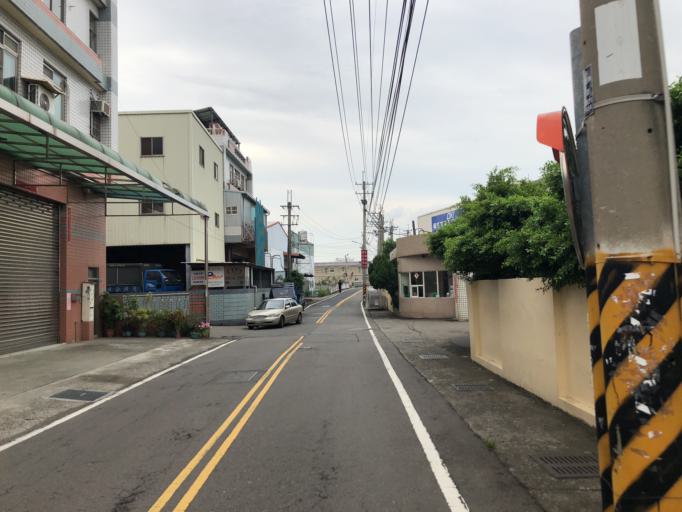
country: TW
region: Taiwan
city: Zhongxing New Village
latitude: 24.0475
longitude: 120.6912
